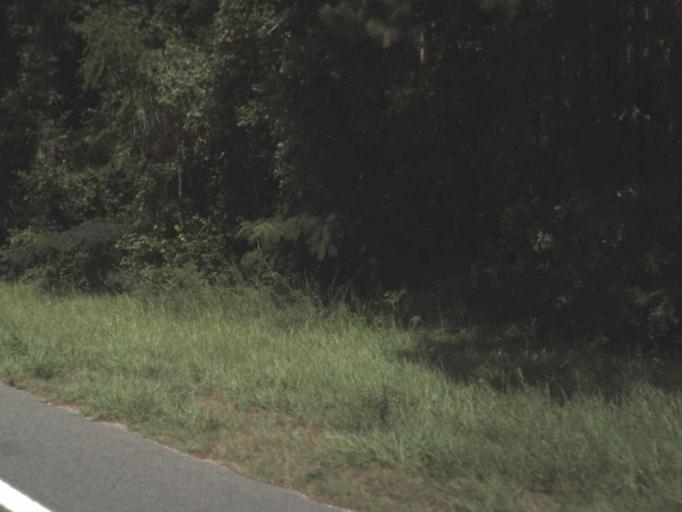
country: US
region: Florida
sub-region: Madison County
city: Madison
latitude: 30.6199
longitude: -83.3273
